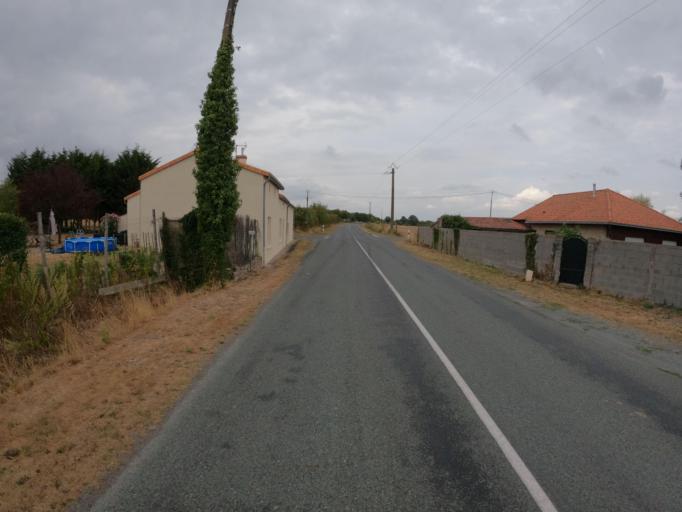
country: FR
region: Pays de la Loire
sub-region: Departement de Maine-et-Loire
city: Le Longeron
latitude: 47.0295
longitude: -1.0468
